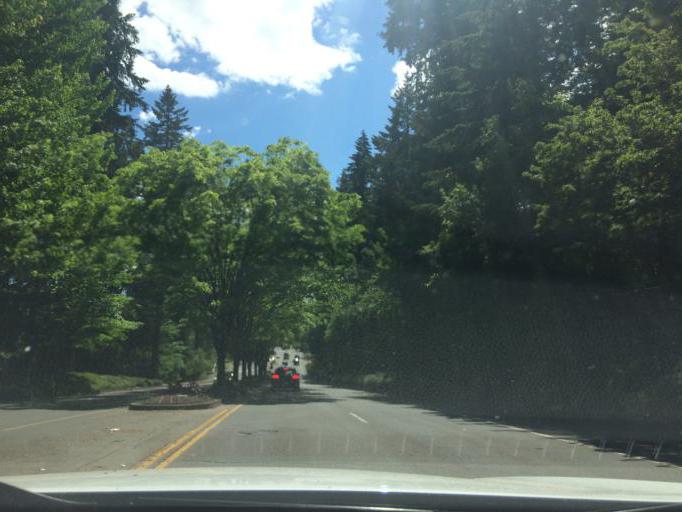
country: US
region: Oregon
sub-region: Washington County
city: Durham
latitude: 45.4040
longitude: -122.7309
